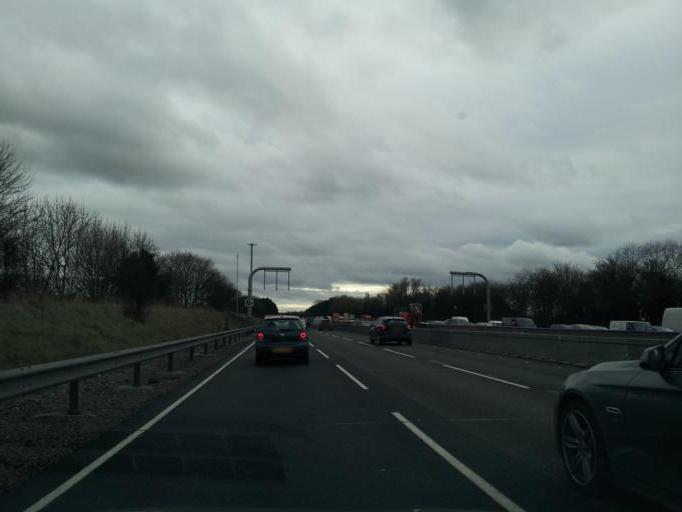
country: GB
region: England
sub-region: Staffordshire
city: Penkridge
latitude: 52.7288
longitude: -2.0989
